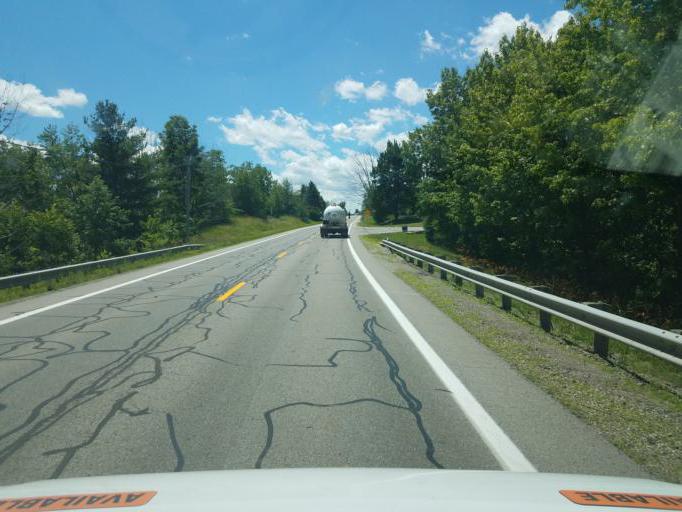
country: US
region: Ohio
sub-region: Crawford County
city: Galion
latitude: 40.6706
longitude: -82.8210
